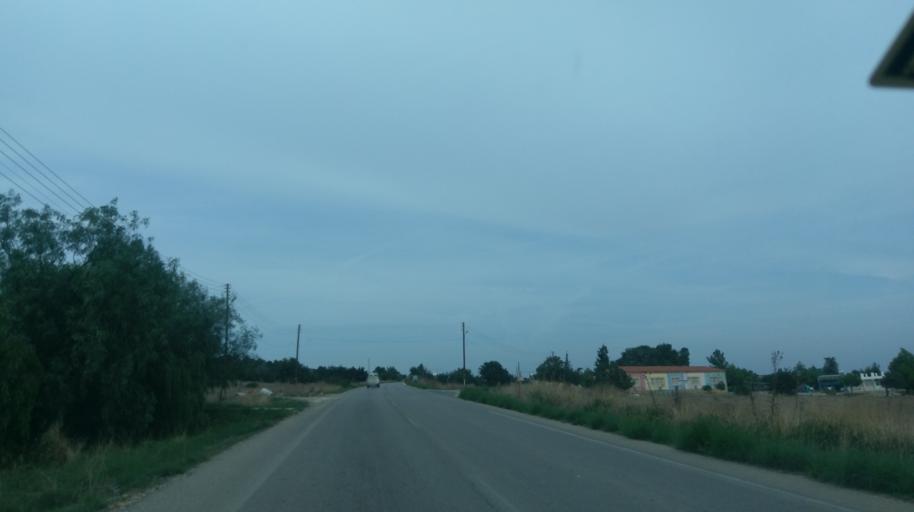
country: CY
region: Ammochostos
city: Leonarisso
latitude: 35.4230
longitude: 34.1260
